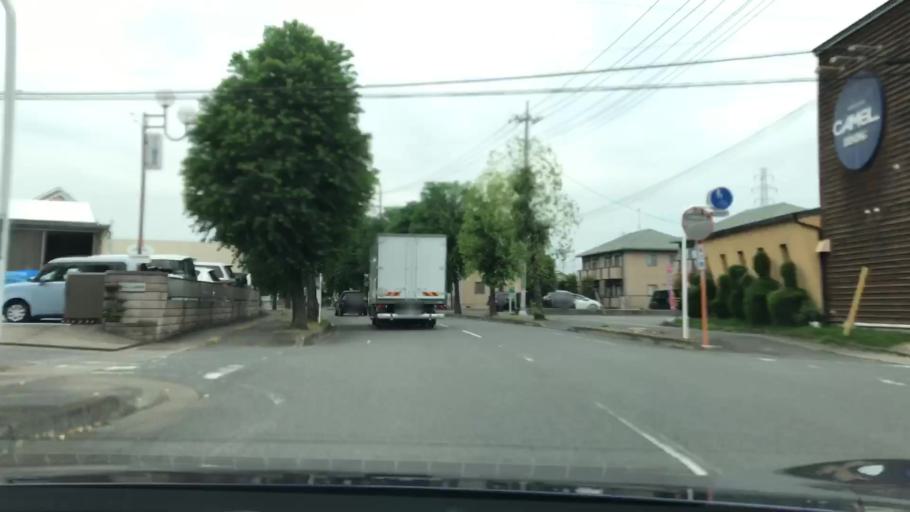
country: JP
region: Gunma
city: Isesaki
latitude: 36.3339
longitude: 139.1562
